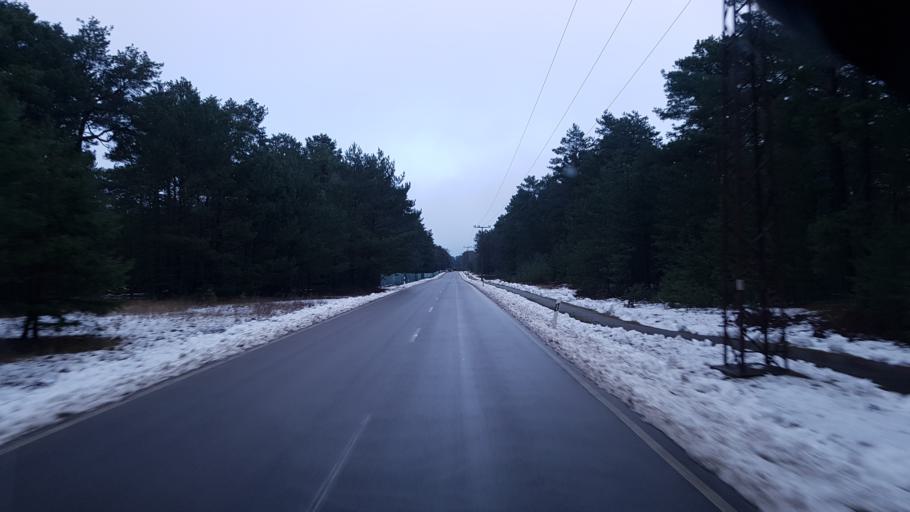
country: DE
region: Brandenburg
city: Janschwalde
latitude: 51.8780
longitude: 14.5154
